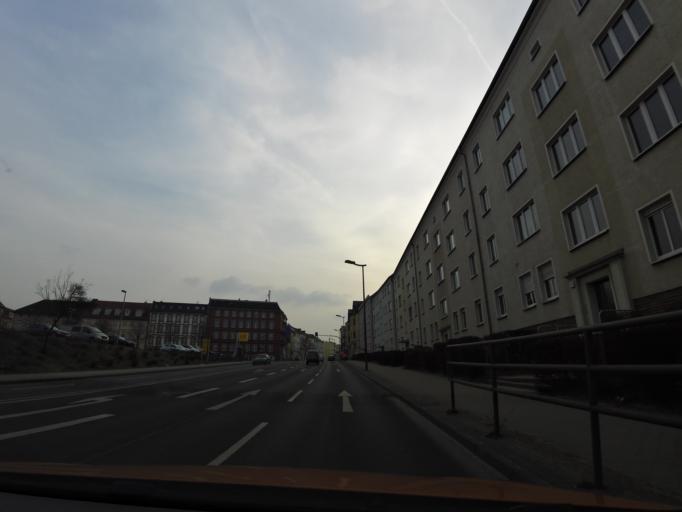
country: DE
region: Brandenburg
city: Frankfurt (Oder)
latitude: 52.3390
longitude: 14.5397
